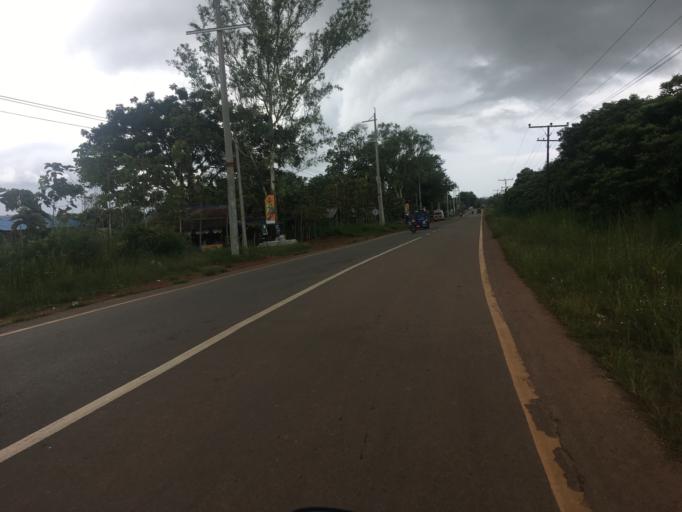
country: MM
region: Mon
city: Mawlamyine
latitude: 16.4556
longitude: 97.6771
